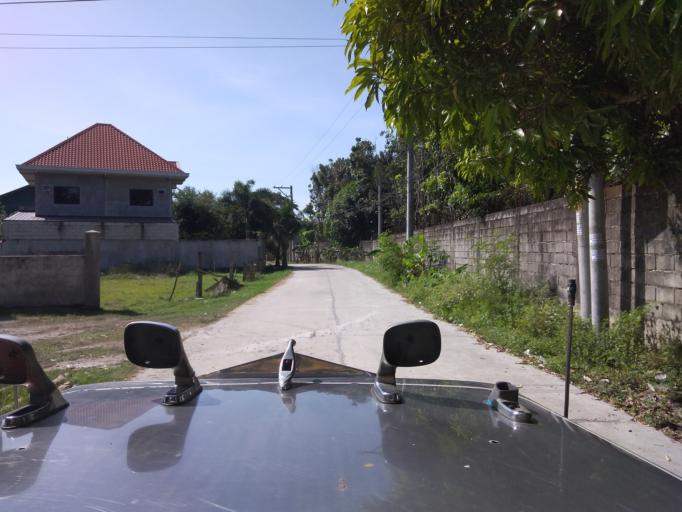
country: PH
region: Central Luzon
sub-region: Province of Pampanga
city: Bacolor
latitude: 15.0048
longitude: 120.6697
